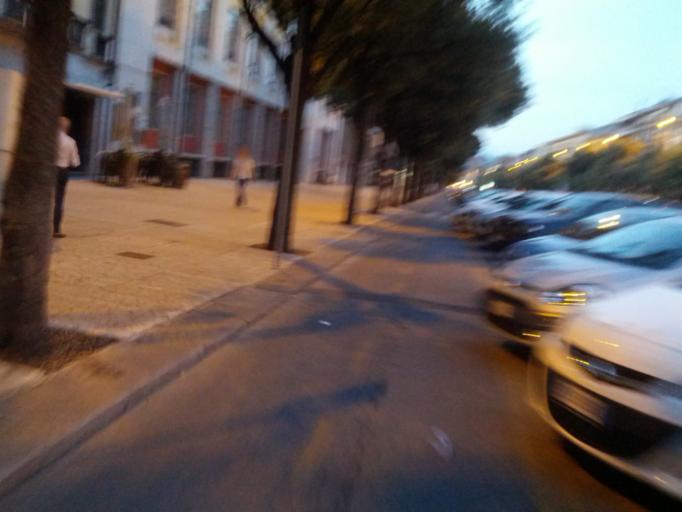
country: IT
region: Veneto
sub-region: Provincia di Verona
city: Verona
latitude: 45.4328
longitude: 10.9887
